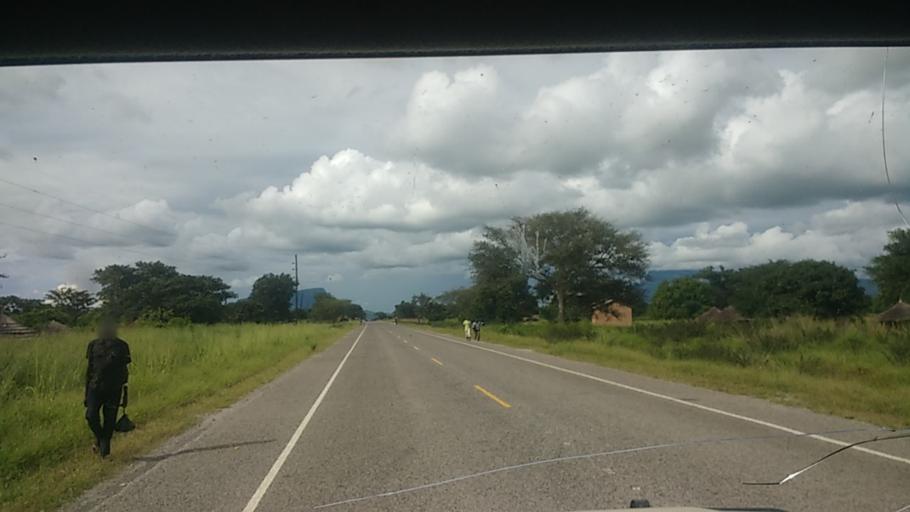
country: UG
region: Eastern Region
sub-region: Katakwi District
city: Katakwi
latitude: 2.0198
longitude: 34.1135
